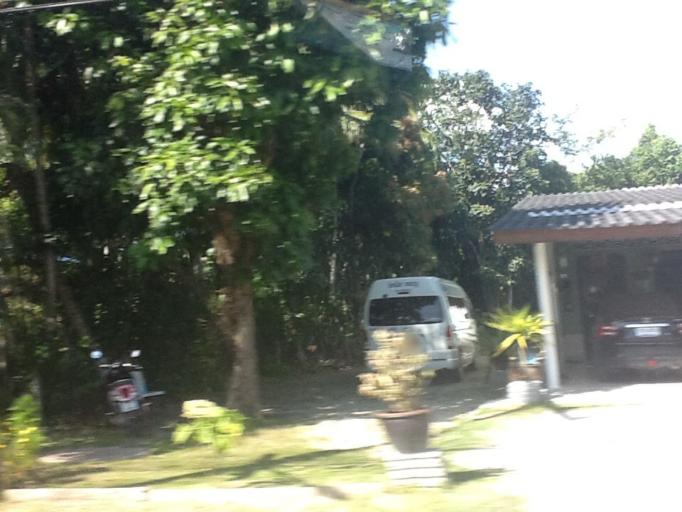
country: TH
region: Phuket
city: Thalang
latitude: 8.1244
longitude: 98.3128
